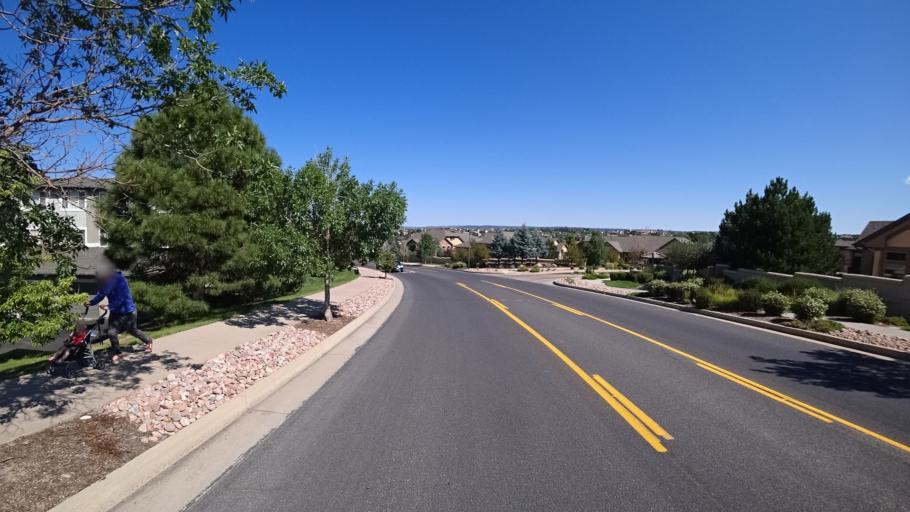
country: US
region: Colorado
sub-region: El Paso County
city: Black Forest
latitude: 38.9682
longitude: -104.7774
